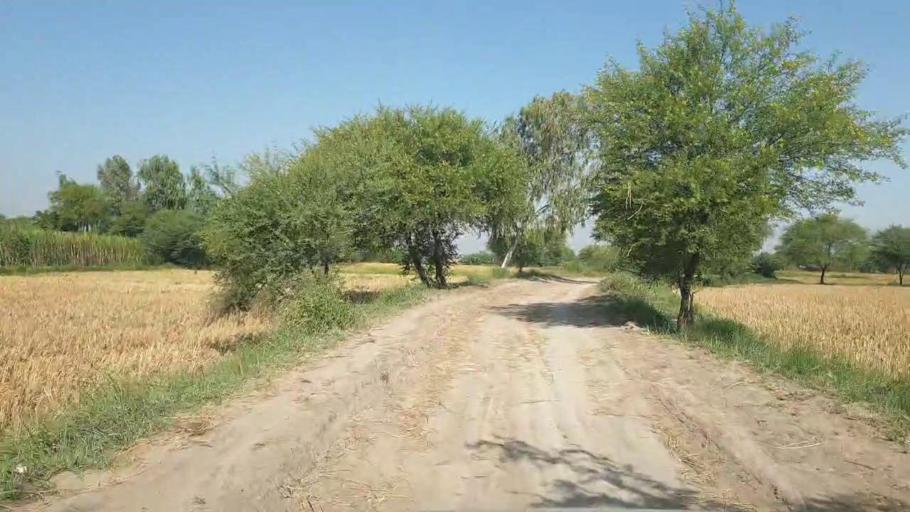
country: PK
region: Sindh
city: Talhar
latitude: 24.8094
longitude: 68.7862
